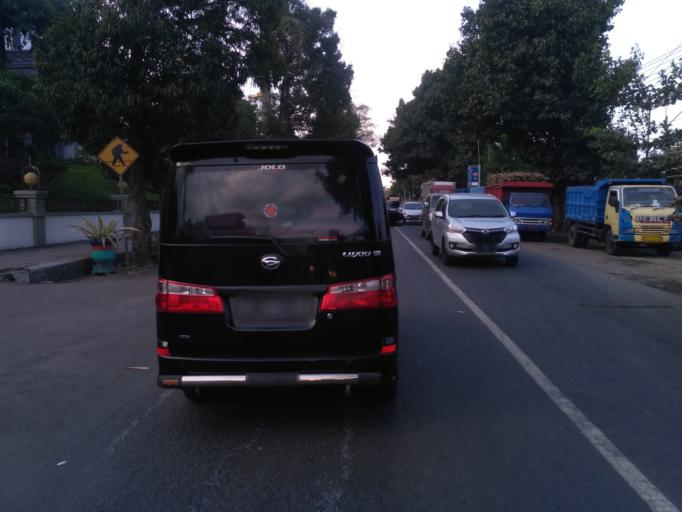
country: ID
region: East Java
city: Kebonsari
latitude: -8.0292
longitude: 112.6152
